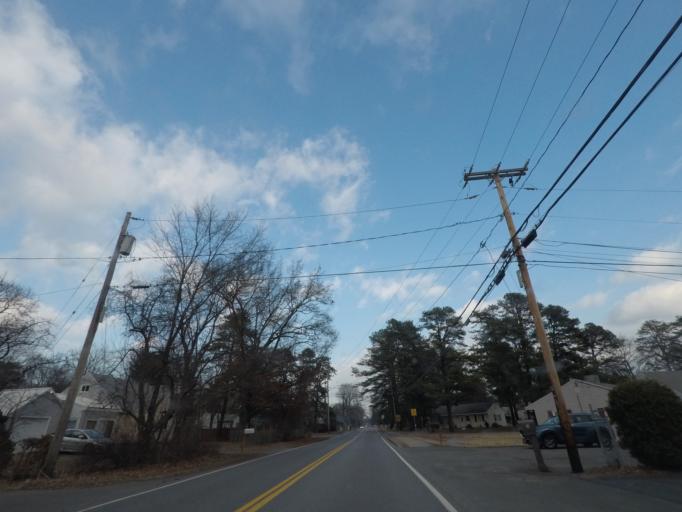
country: US
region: New York
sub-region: Albany County
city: Colonie
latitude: 42.7106
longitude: -73.8383
